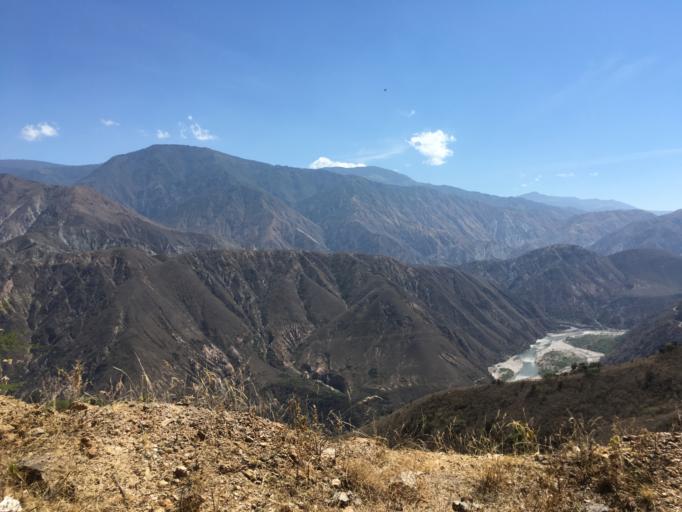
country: CO
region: Santander
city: Aratoca
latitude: 6.7850
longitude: -72.9962
